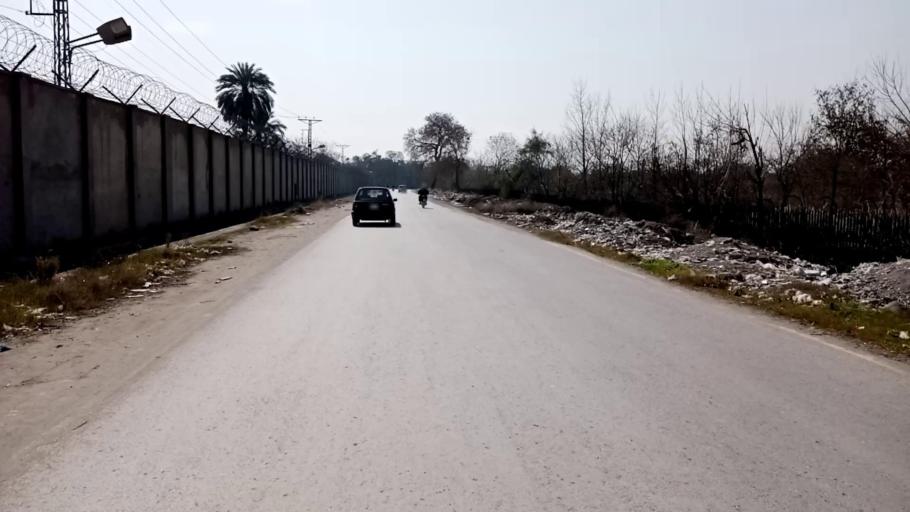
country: PK
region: Khyber Pakhtunkhwa
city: Peshawar
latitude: 33.9938
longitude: 71.5106
